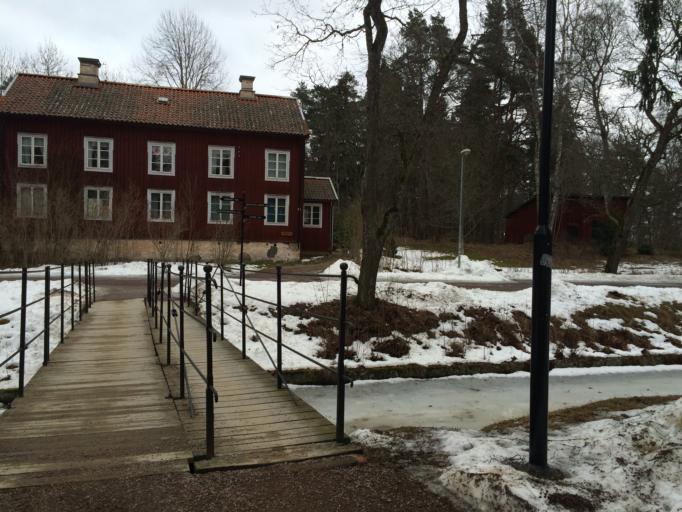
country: SE
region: Vaestmanland
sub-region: Hallstahammars Kommun
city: Hallstahammar
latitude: 59.6113
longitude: 16.2113
